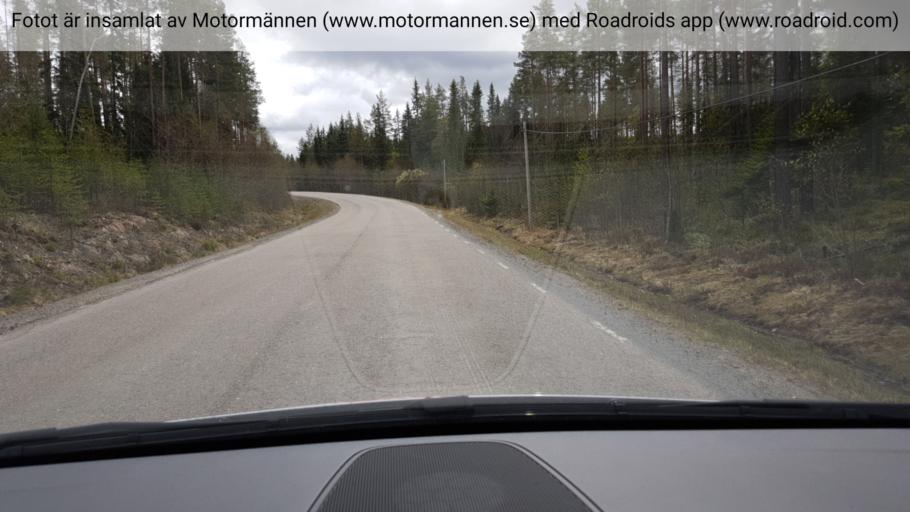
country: SE
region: Jaemtland
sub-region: Bergs Kommun
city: Hoverberg
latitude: 62.6651
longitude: 14.7607
